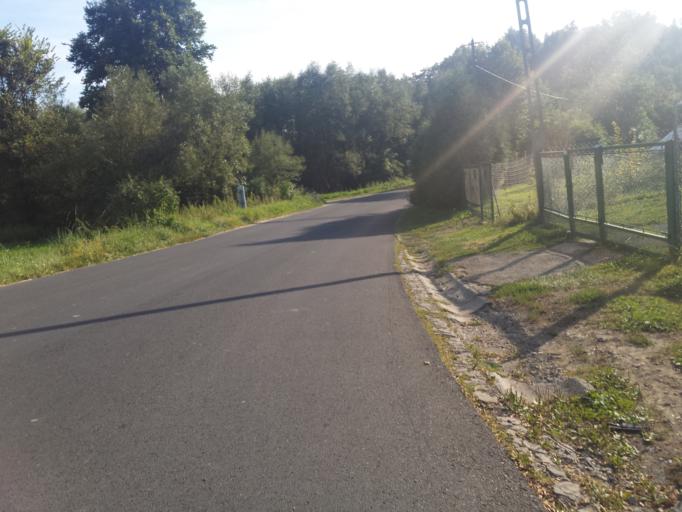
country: PL
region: Subcarpathian Voivodeship
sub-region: Powiat leski
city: Uherce Mineralne
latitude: 49.4629
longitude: 22.3980
